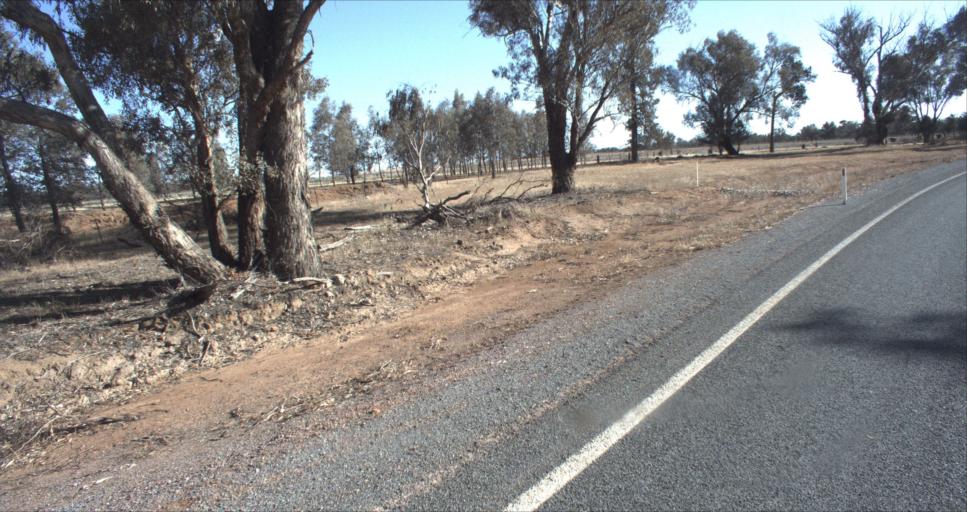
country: AU
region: New South Wales
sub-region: Leeton
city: Leeton
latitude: -34.6434
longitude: 146.3565
